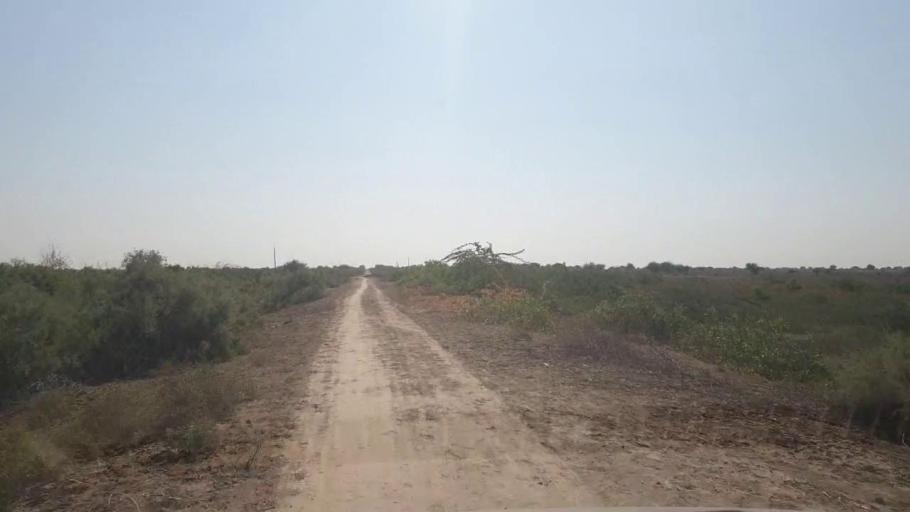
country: PK
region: Sindh
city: Tando Bago
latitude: 24.8959
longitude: 69.1645
